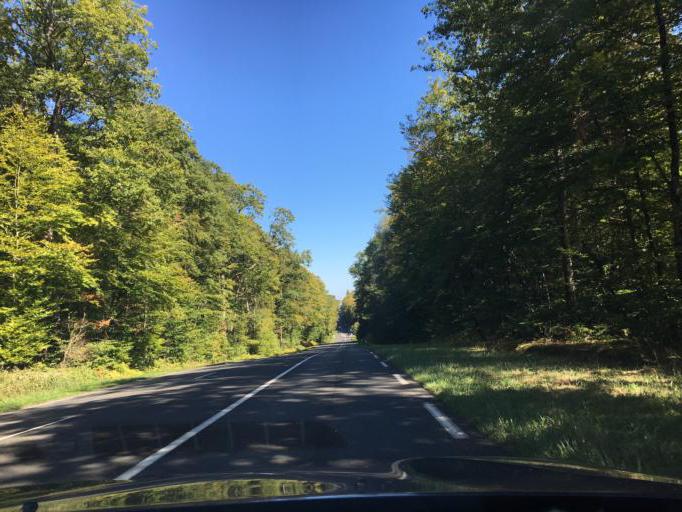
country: FR
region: Centre
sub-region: Departement d'Indre-et-Loire
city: Cheille
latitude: 47.2426
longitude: 0.4309
